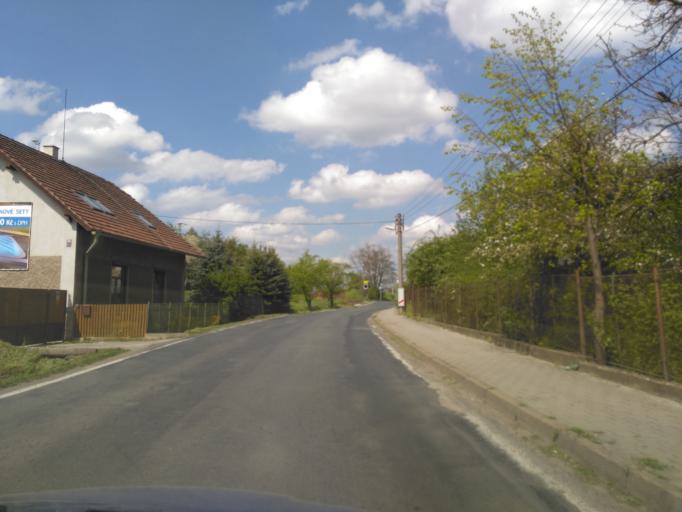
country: CZ
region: Central Bohemia
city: Lochovice
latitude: 49.8747
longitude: 13.9935
